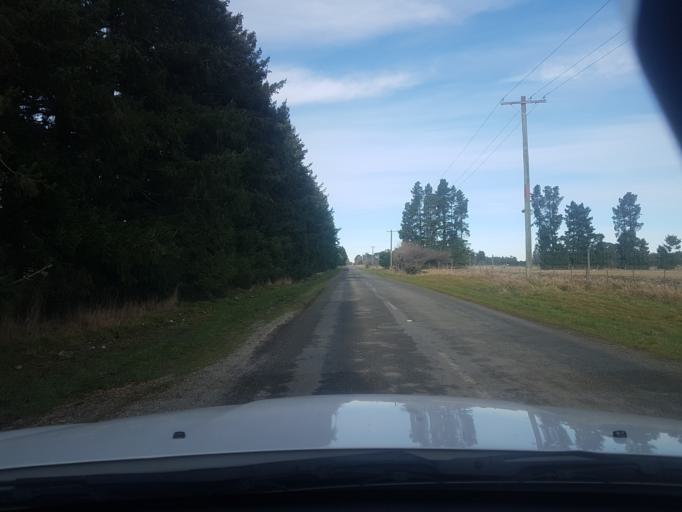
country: NZ
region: Canterbury
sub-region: Timaru District
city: Pleasant Point
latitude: -43.9593
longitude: 171.2660
